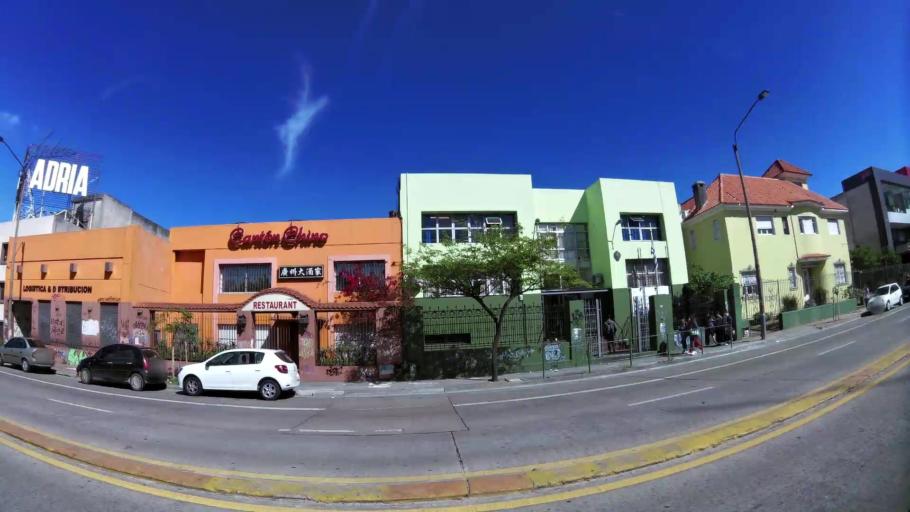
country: UY
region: Montevideo
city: Montevideo
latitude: -34.8907
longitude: -56.1612
